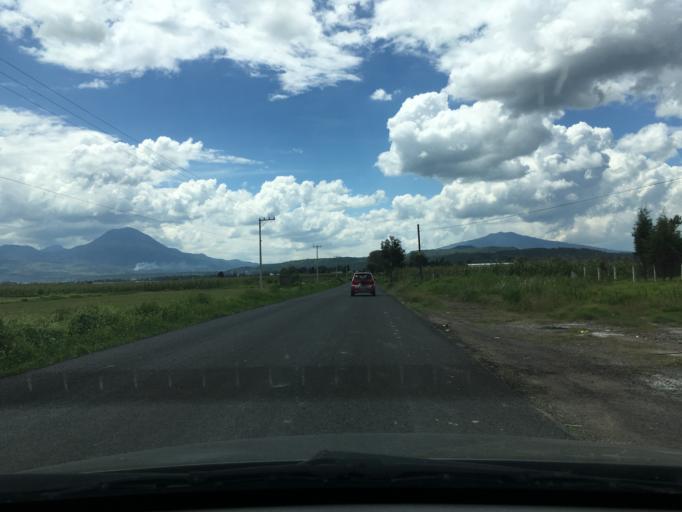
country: MX
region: Michoacan
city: Zacapu
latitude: 19.8405
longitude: -101.7472
